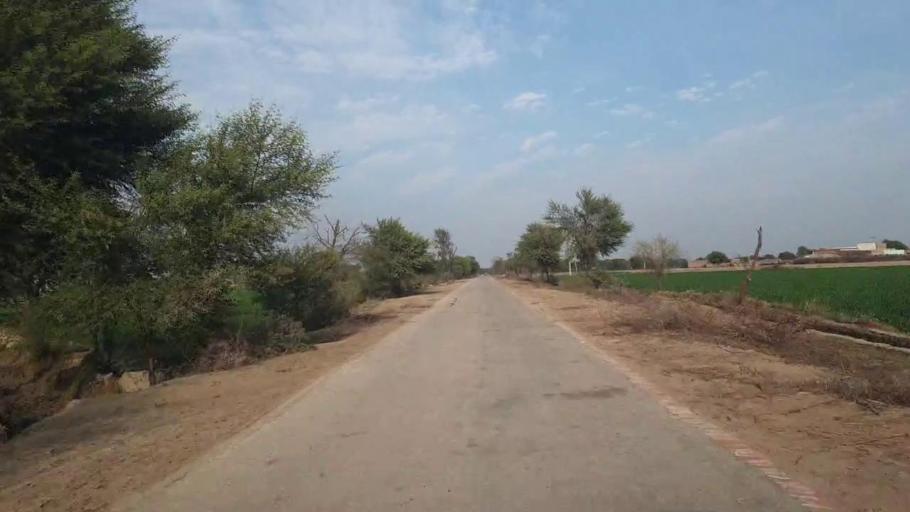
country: PK
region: Sindh
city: Shahdadpur
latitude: 26.0455
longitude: 68.5623
